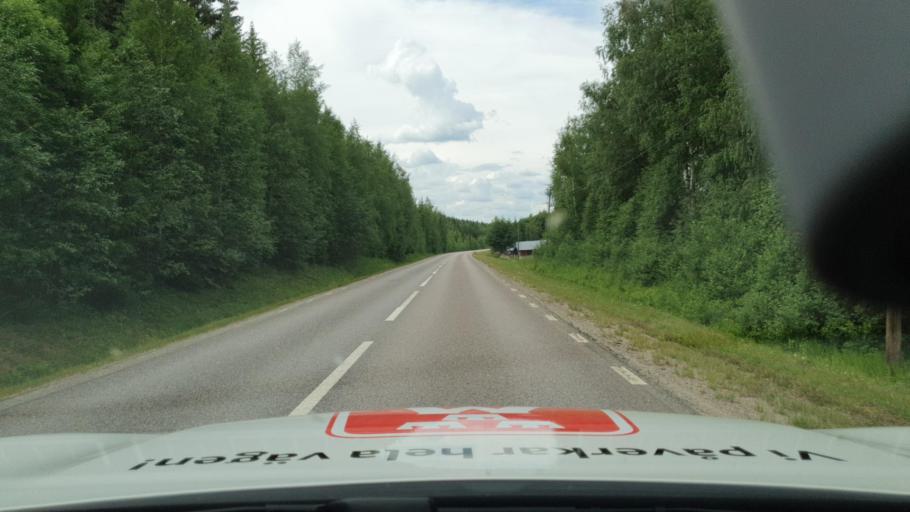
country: NO
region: Hedmark
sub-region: Trysil
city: Innbygda
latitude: 60.9024
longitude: 12.5718
